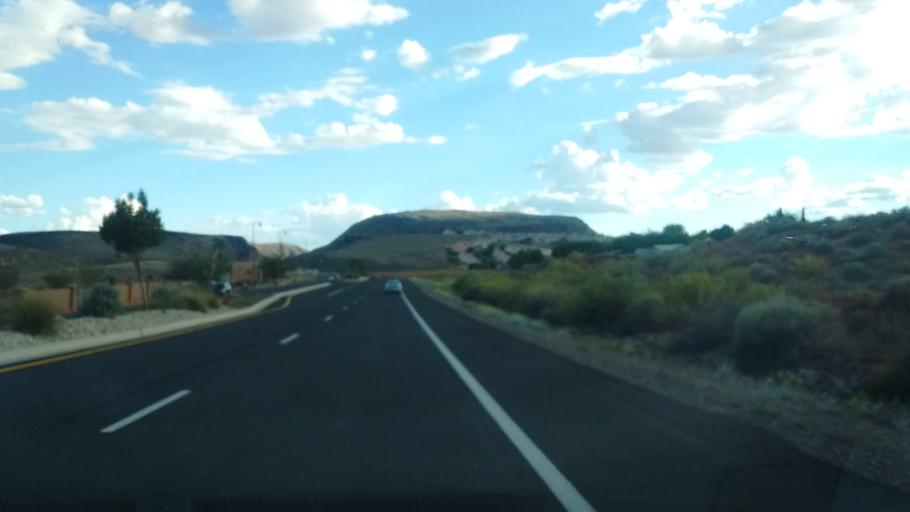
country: US
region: Utah
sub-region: Washington County
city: Washington
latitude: 37.1361
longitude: -113.4857
